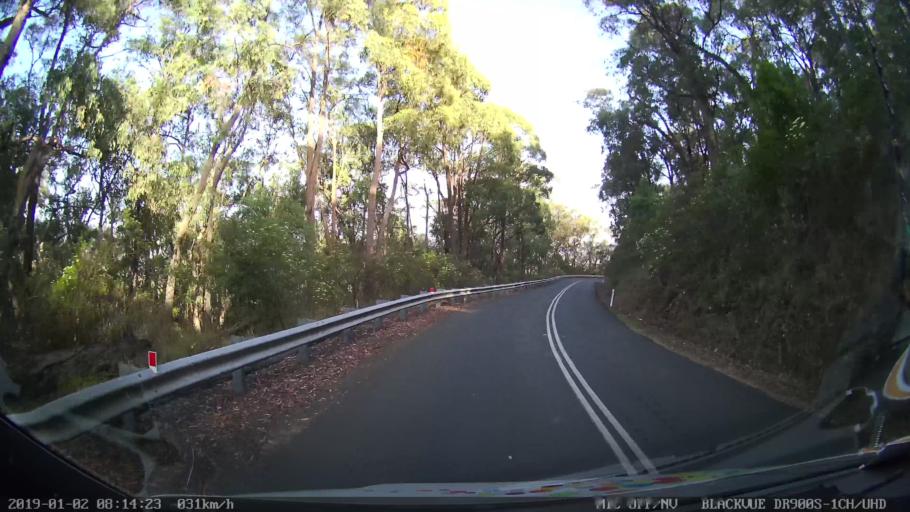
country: AU
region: New South Wales
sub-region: Tumut Shire
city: Tumut
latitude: -35.5864
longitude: 148.3396
